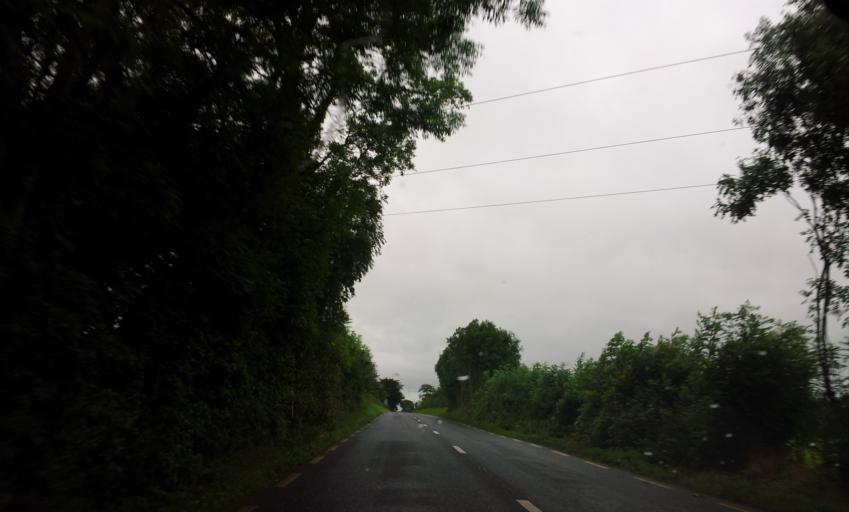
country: IE
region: Munster
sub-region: County Cork
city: Mitchelstown
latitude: 52.2577
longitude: -8.3433
